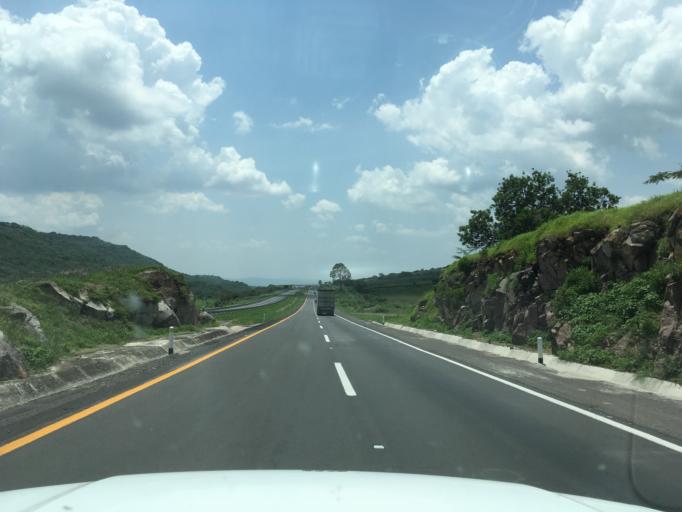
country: MX
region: Jalisco
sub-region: Zapotlan del Rey
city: Zapotlan del Rey
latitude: 20.5218
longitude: -102.9932
